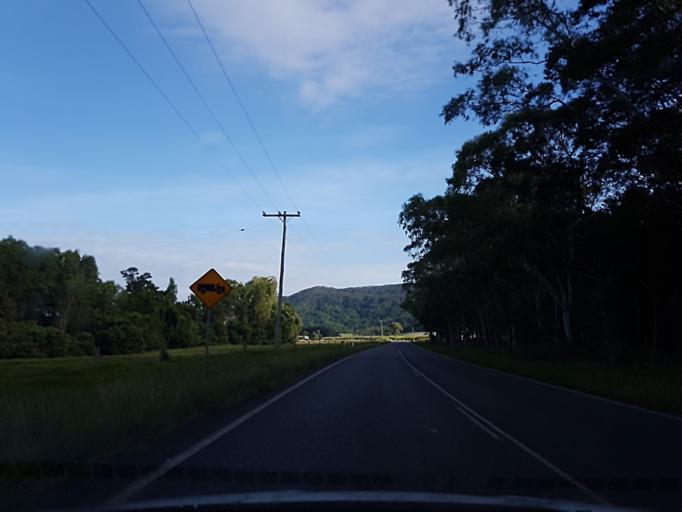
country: AU
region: Queensland
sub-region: Cairns
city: Port Douglas
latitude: -16.3384
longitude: 145.4104
